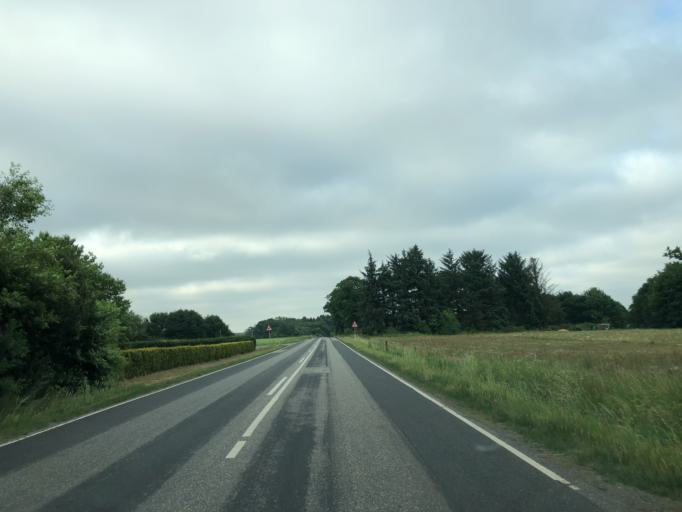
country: DK
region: South Denmark
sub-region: Vejle Kommune
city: Give
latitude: 55.8881
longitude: 9.2167
